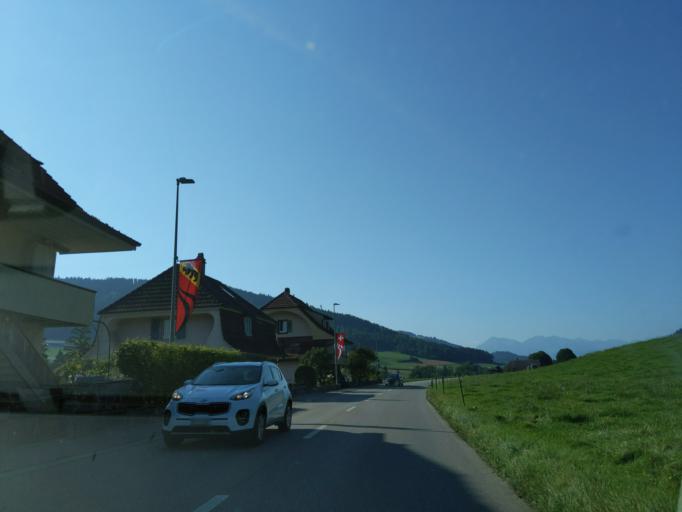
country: CH
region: Bern
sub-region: Bern-Mittelland District
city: Konolfingen
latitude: 46.8684
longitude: 7.6231
